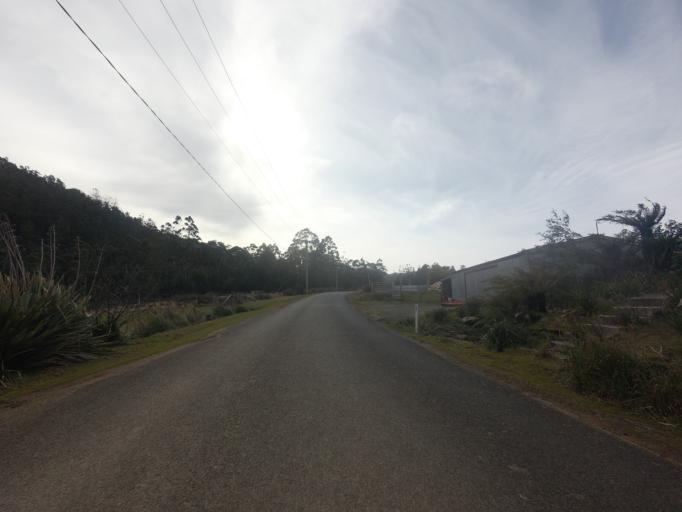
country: AU
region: Tasmania
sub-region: Huon Valley
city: Huonville
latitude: -43.0512
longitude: 147.1073
